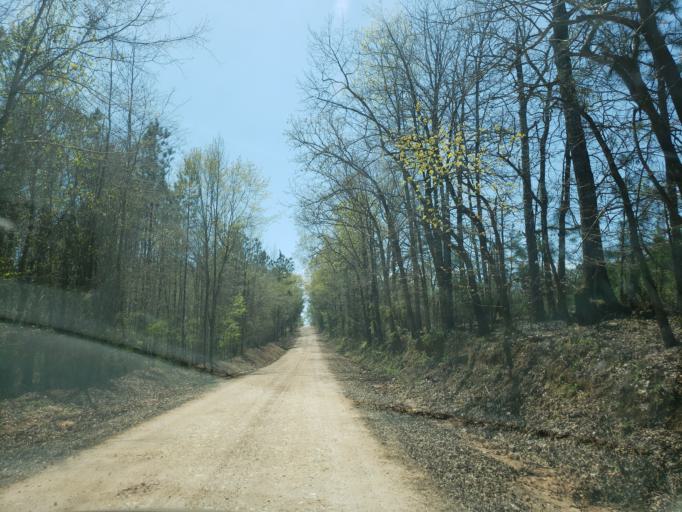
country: US
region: Alabama
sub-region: Tallapoosa County
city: Camp Hill
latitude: 32.6636
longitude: -85.6622
